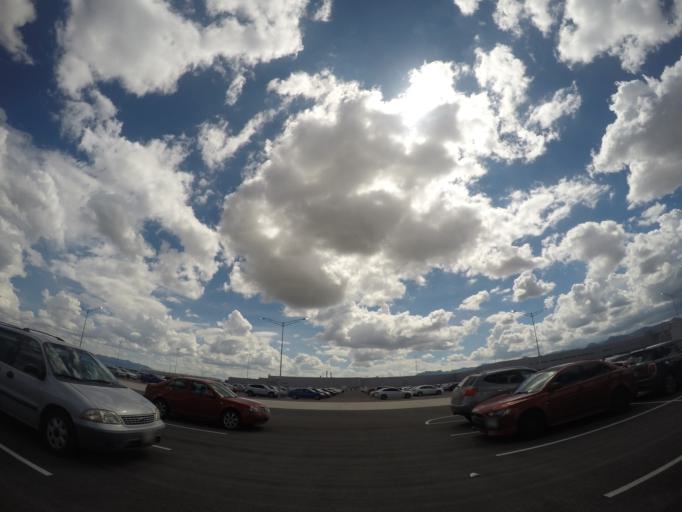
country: MX
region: San Luis Potosi
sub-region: Zaragoza
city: Cerro Gordo
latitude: 21.9673
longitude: -100.8465
